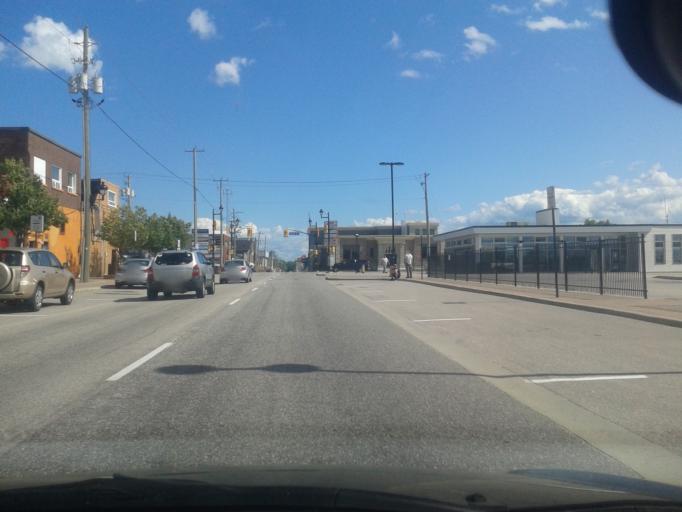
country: CA
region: Ontario
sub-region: Nipissing District
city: North Bay
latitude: 46.3092
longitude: -79.4640
